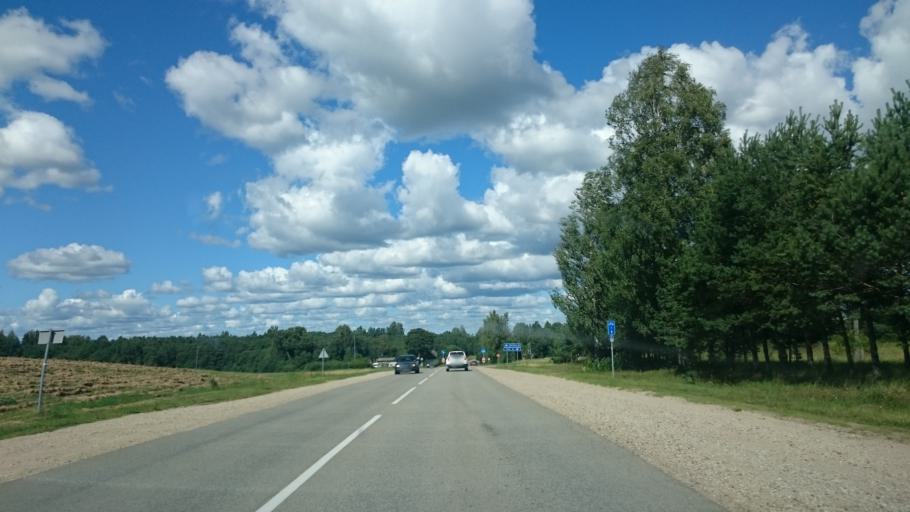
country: LV
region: Kuldigas Rajons
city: Kuldiga
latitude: 56.9574
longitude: 21.9445
